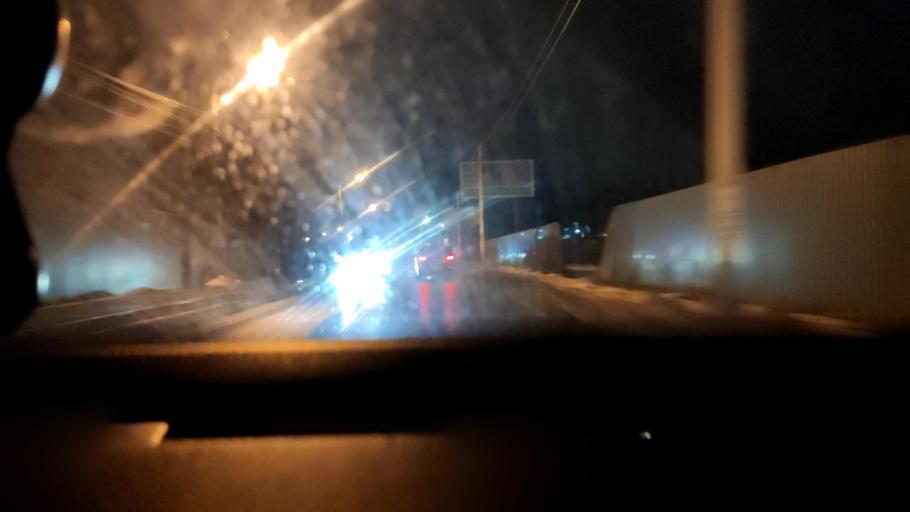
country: RU
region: Moskovskaya
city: Zhukovskiy
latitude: 55.5885
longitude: 38.1034
